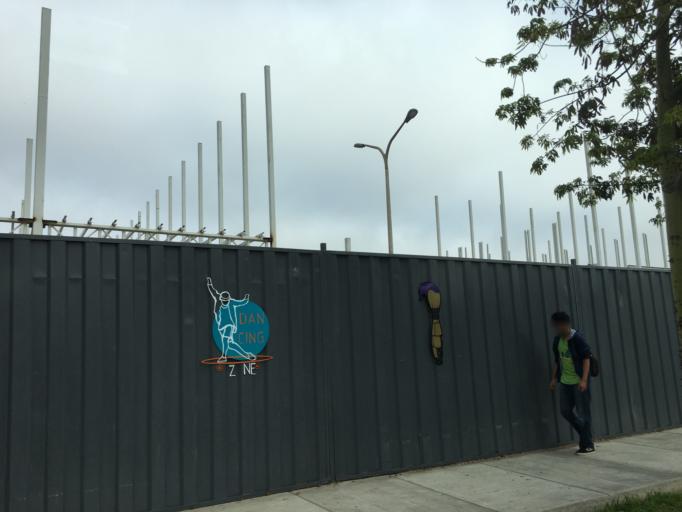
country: PE
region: Callao
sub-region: Callao
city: Callao
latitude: -12.0702
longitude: -77.0786
